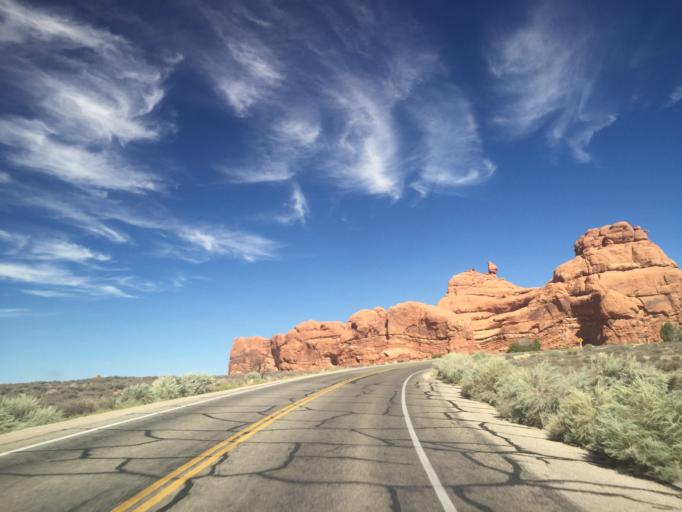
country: US
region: Utah
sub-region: Grand County
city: Moab
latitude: 38.6948
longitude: -109.5518
